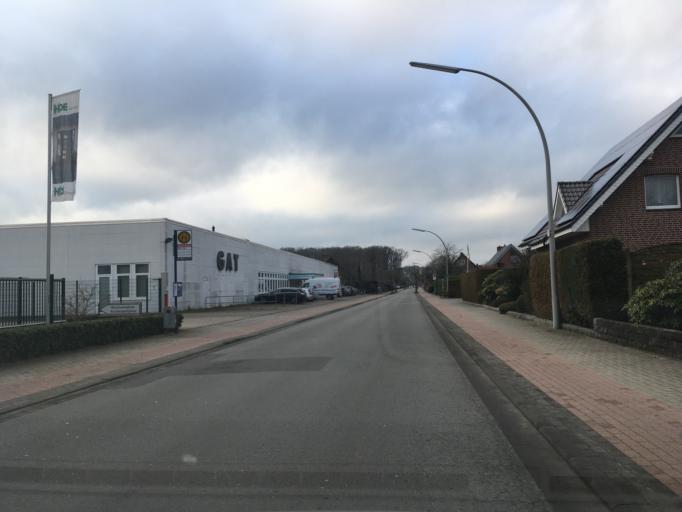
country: DE
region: North Rhine-Westphalia
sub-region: Regierungsbezirk Munster
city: Gescher
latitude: 51.9482
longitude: 7.0102
